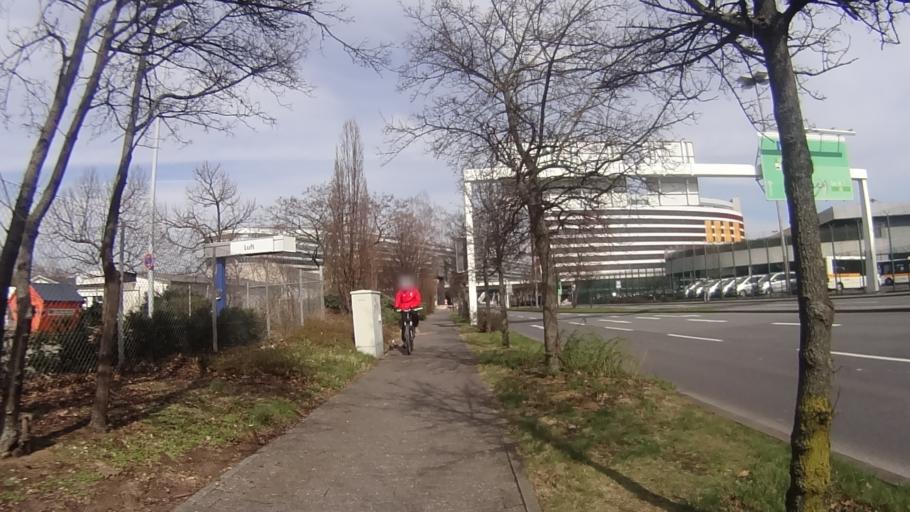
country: DE
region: Hesse
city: Kelsterbach
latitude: 50.0499
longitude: 8.5626
